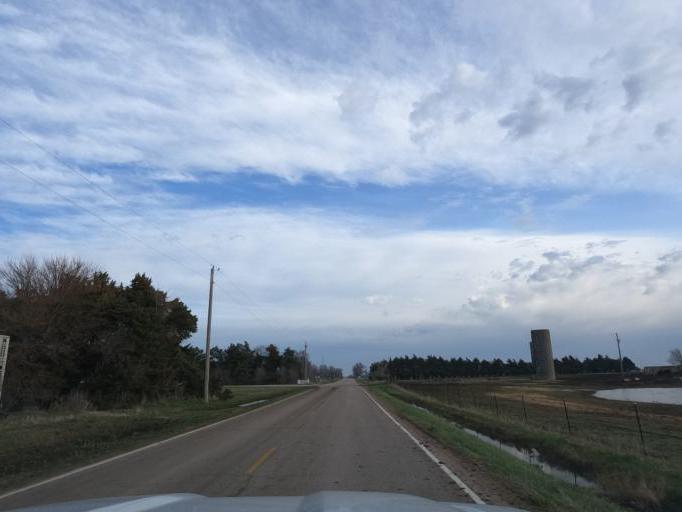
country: US
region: Kansas
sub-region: Reno County
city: Nickerson
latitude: 38.0099
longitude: -98.1789
